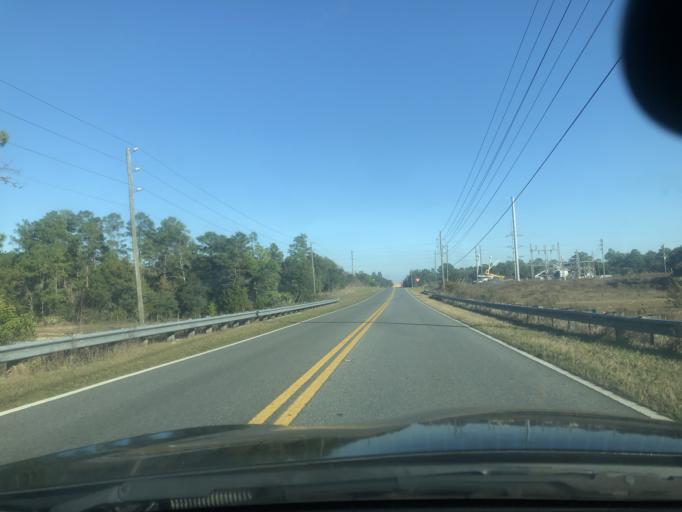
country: US
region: Florida
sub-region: Citrus County
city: Sugarmill Woods
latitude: 28.7640
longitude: -82.5198
